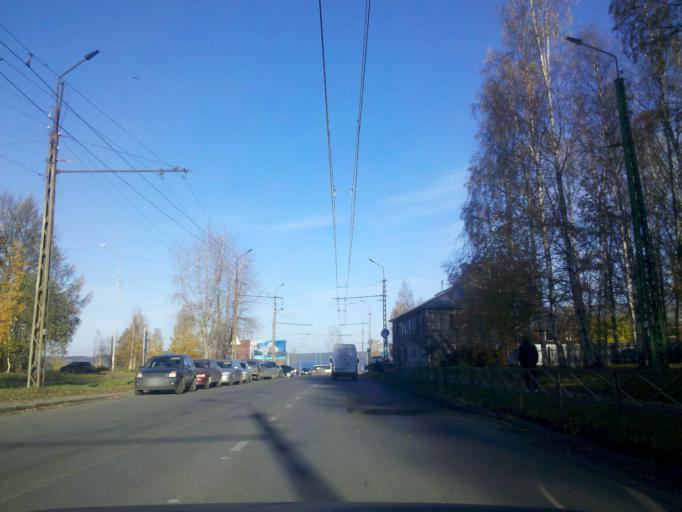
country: RU
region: Republic of Karelia
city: Petrozavodsk
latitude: 61.7986
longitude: 34.3582
